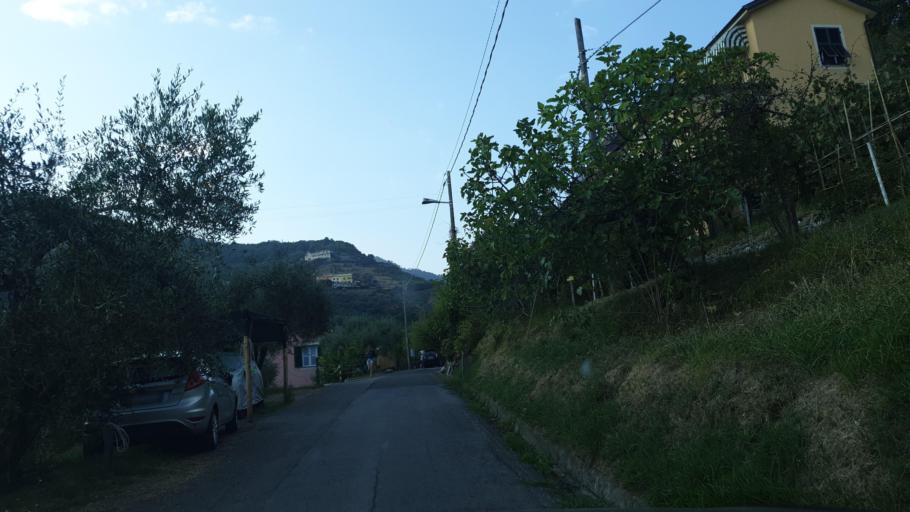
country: IT
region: Liguria
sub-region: Provincia di La Spezia
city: Levanto
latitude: 44.1798
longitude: 9.6186
